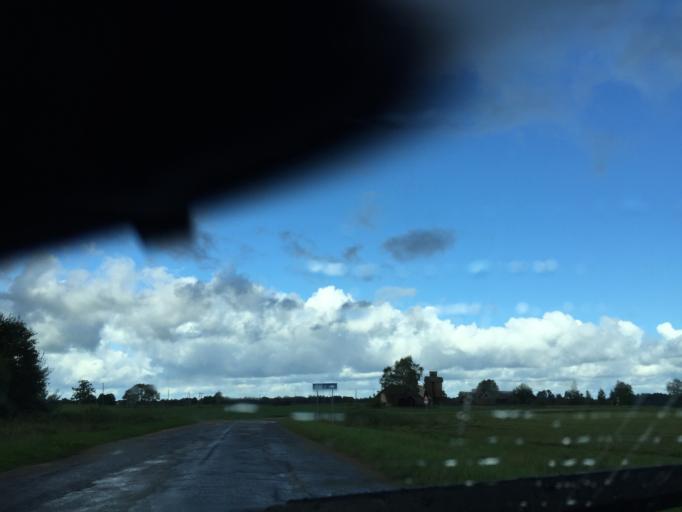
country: LV
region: Talsu Rajons
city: Sabile
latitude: 57.0540
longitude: 22.4673
